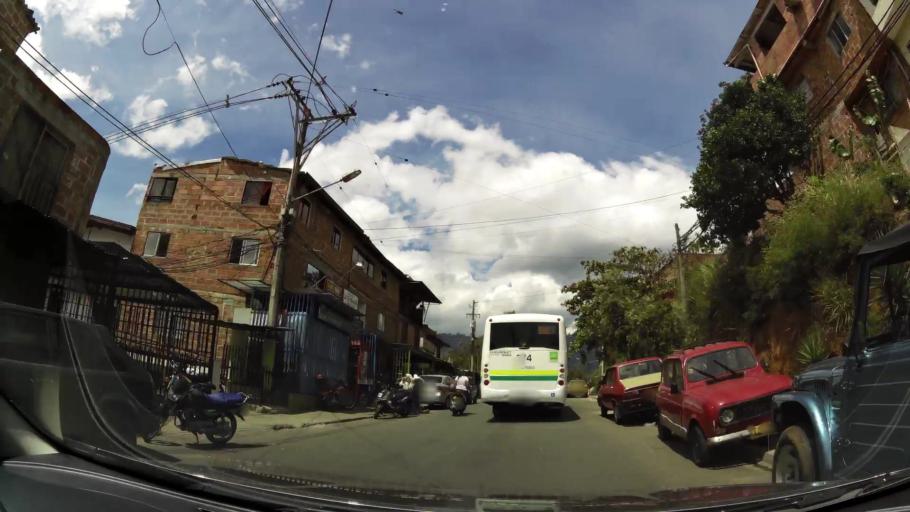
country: CO
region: Antioquia
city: Bello
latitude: 6.3476
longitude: -75.5527
